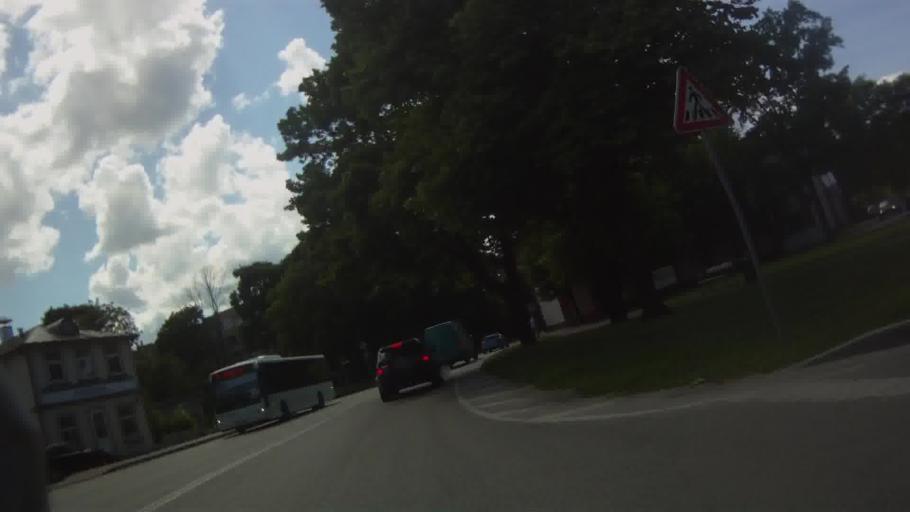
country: LV
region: Jurmala
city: Jurmala
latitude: 56.9687
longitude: 23.7744
